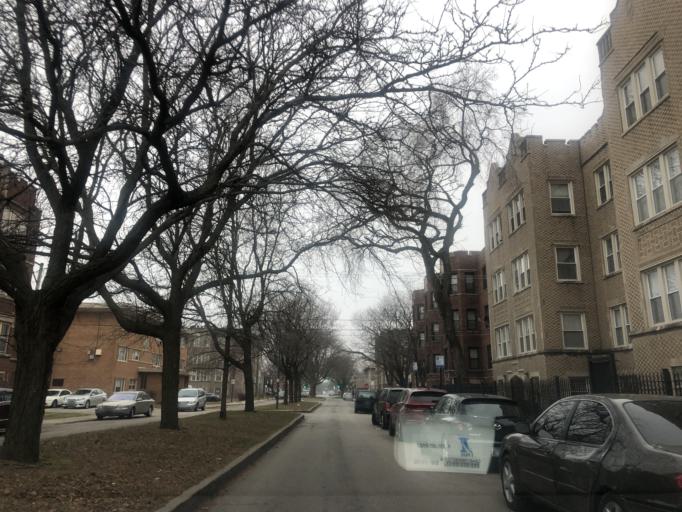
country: US
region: Illinois
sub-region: Cook County
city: Evergreen Park
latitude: 41.7476
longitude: -87.6124
